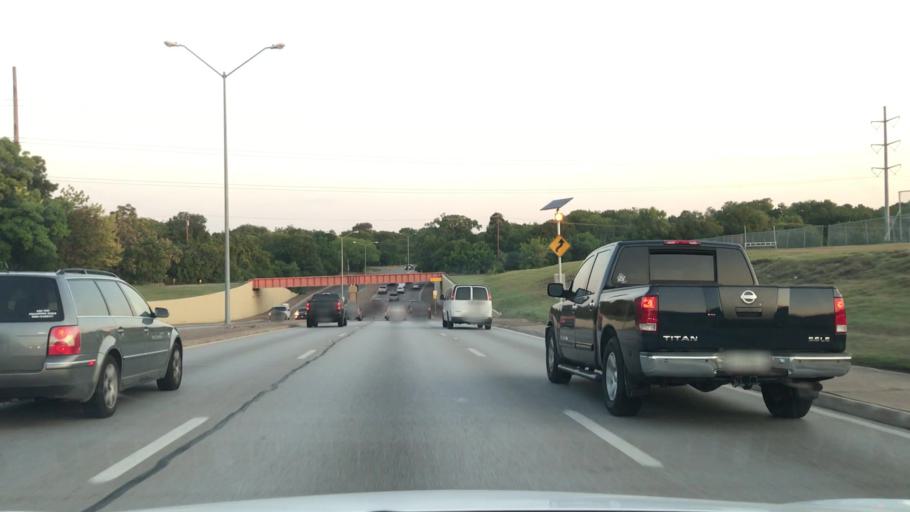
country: US
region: Texas
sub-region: Dallas County
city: Highland Park
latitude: 32.8230
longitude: -96.6945
